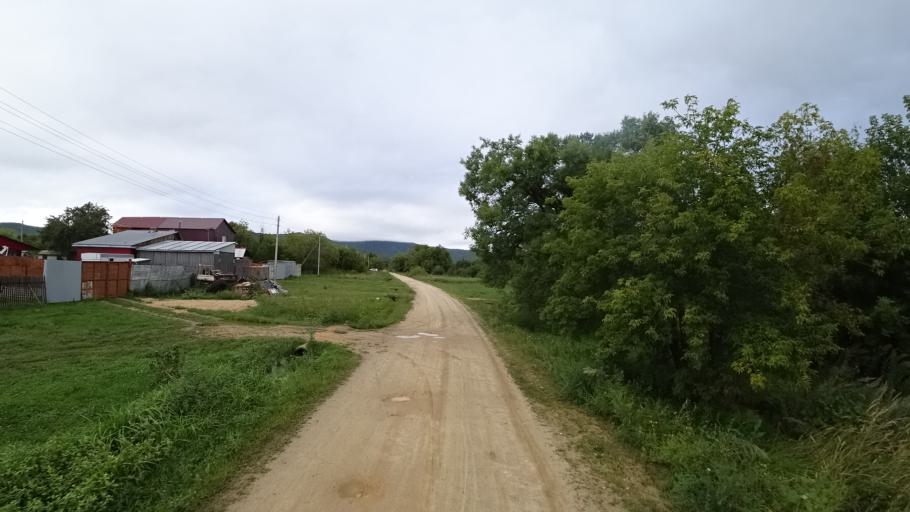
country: RU
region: Primorskiy
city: Rettikhovka
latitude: 44.1341
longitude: 132.6440
